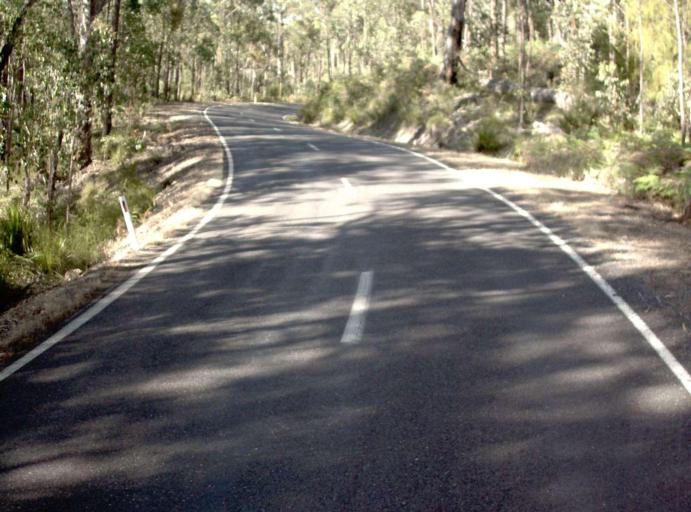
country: AU
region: Victoria
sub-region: East Gippsland
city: Lakes Entrance
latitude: -37.5768
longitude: 148.5455
